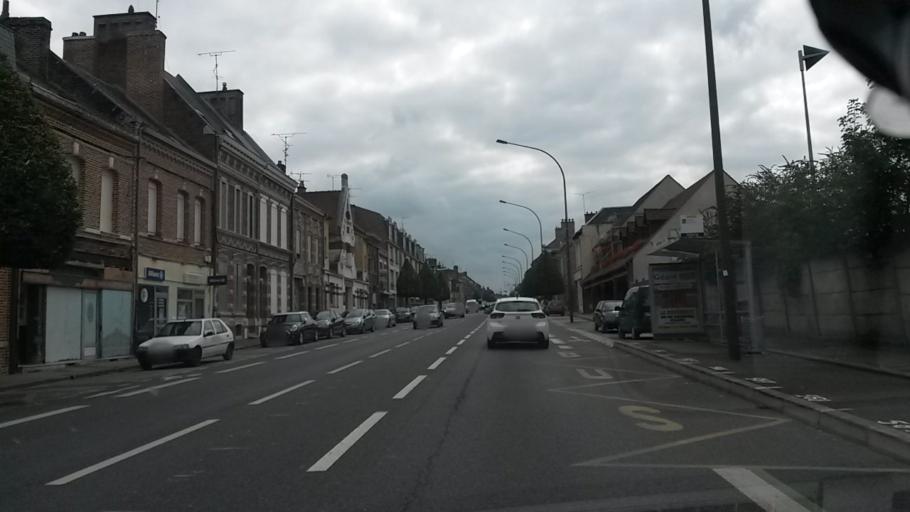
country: FR
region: Picardie
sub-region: Departement de la Somme
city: Amiens
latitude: 49.8921
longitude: 2.2840
